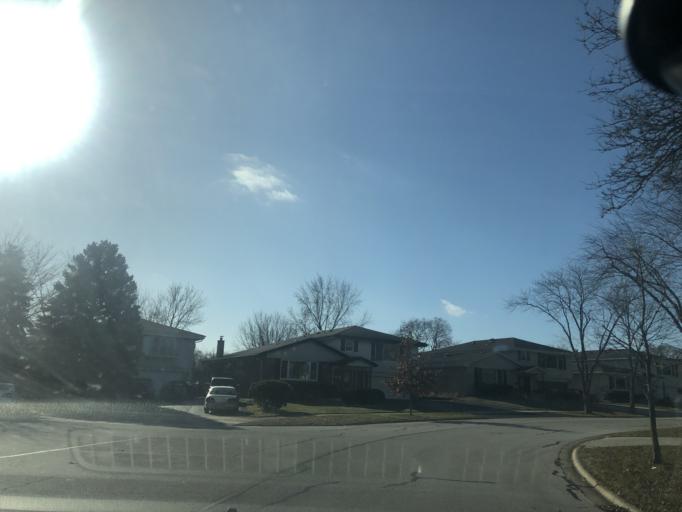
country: US
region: Illinois
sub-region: DuPage County
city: Addison
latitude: 41.9275
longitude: -88.0089
